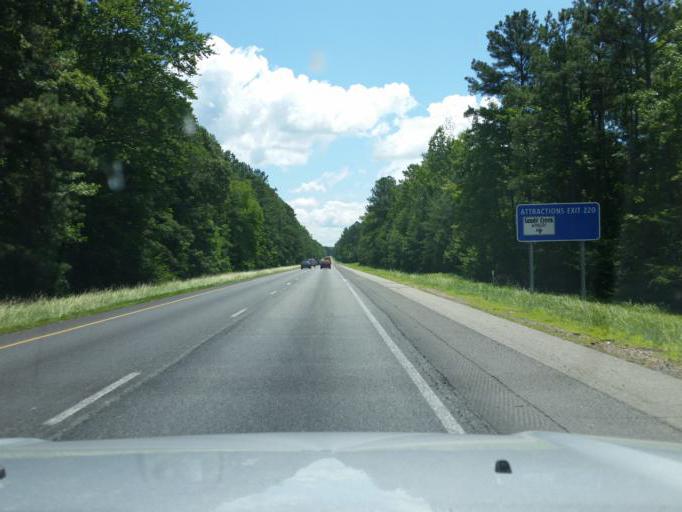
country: US
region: Virginia
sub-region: New Kent County
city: New Kent
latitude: 37.4856
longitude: -76.9544
